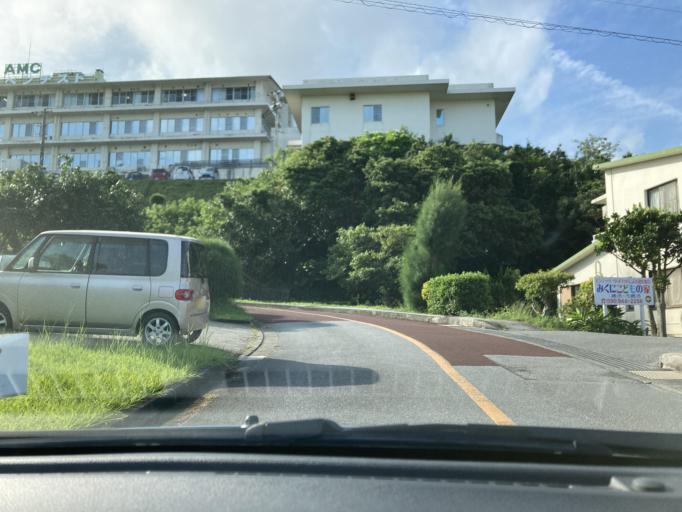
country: JP
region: Okinawa
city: Ginowan
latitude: 26.2296
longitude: 127.7401
